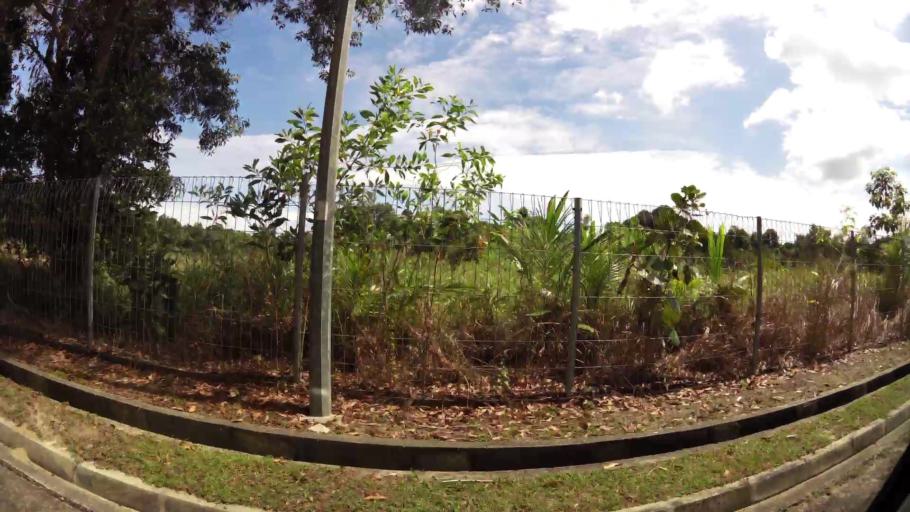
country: BN
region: Brunei and Muara
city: Bandar Seri Begawan
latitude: 4.9364
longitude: 114.8906
